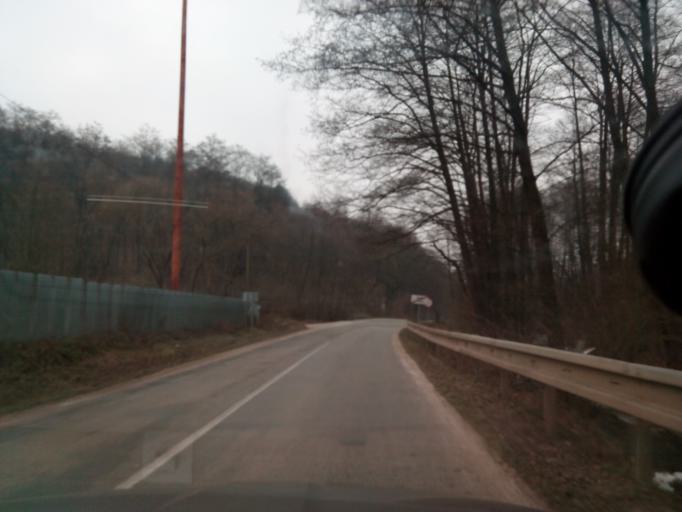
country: SK
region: Kosicky
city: Medzev
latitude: 48.6939
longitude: 20.9465
